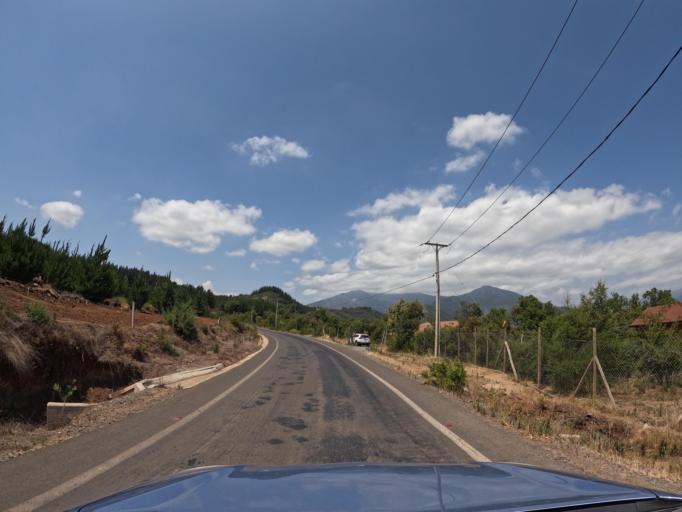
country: CL
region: Maule
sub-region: Provincia de Curico
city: Molina
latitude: -35.1778
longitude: -71.1059
